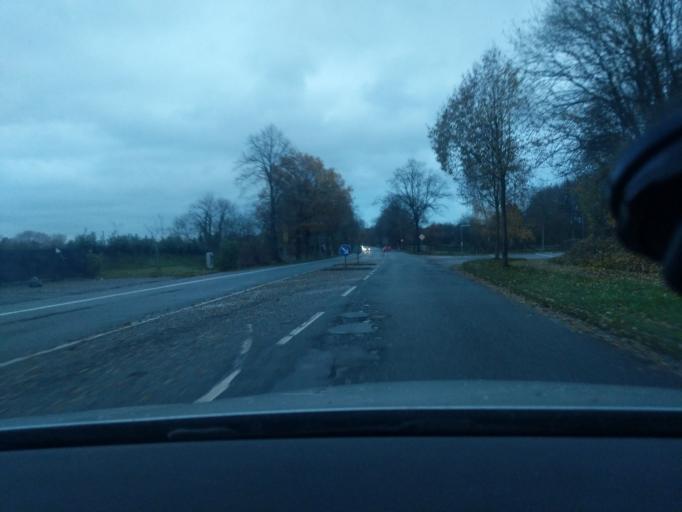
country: DE
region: North Rhine-Westphalia
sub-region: Regierungsbezirk Arnsberg
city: Hamm
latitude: 51.6978
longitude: 7.8822
